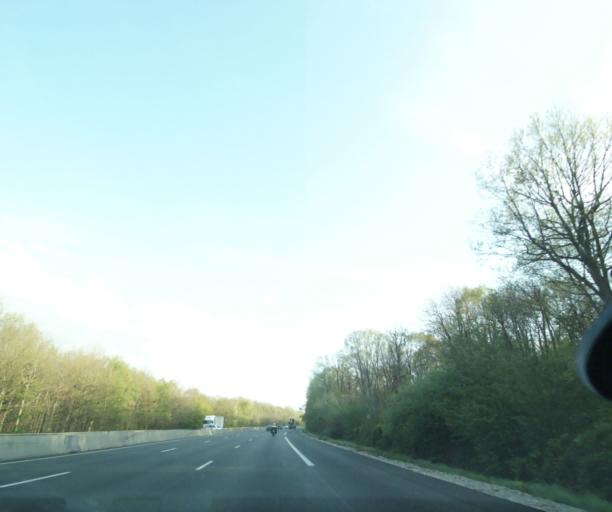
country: FR
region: Ile-de-France
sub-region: Departement de l'Essonne
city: Soisy-sur-Ecole
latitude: 48.5042
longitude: 2.5123
